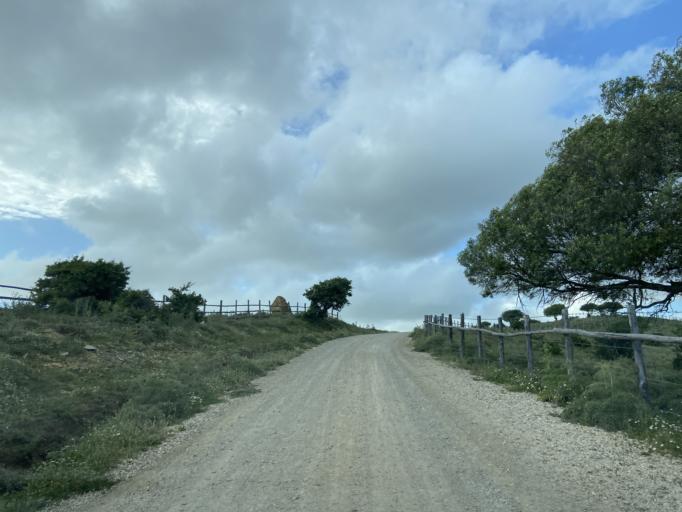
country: IT
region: Latium
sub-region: Citta metropolitana di Roma Capitale
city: Santa Marinella
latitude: 42.0874
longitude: 11.8516
